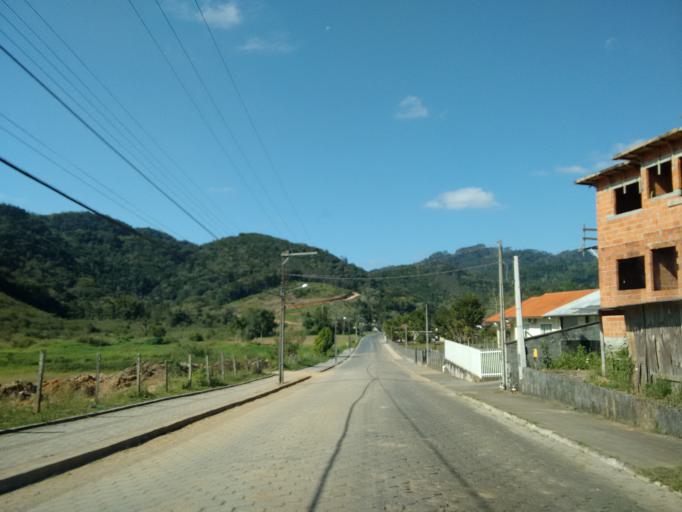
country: BR
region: Santa Catarina
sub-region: Pomerode
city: Pomerode
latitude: -26.7387
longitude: -49.1690
